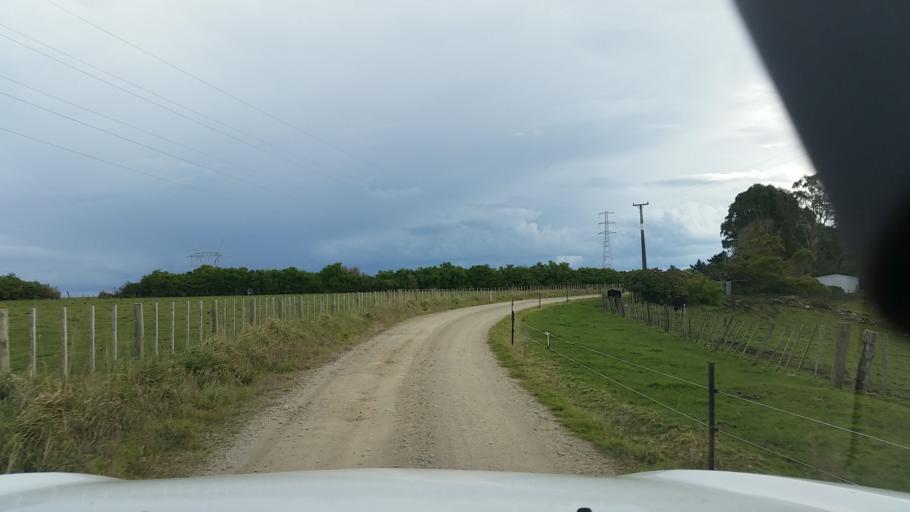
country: NZ
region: Taranaki
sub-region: South Taranaki District
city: Patea
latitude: -39.7896
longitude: 174.7481
